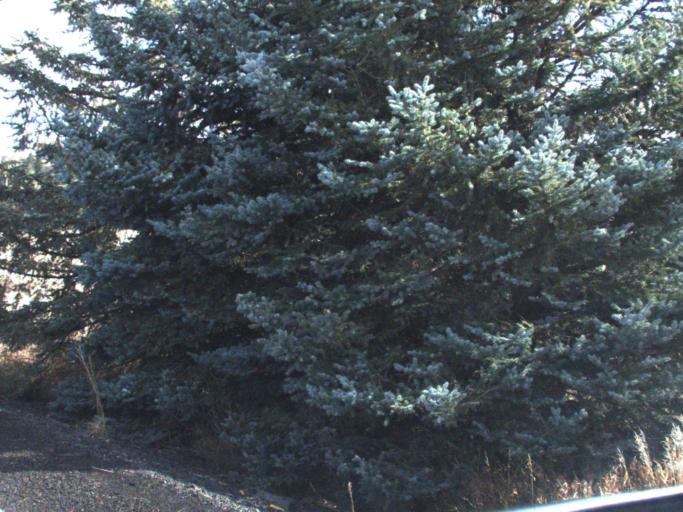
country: US
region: Idaho
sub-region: Latah County
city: Moscow
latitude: 46.9163
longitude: -117.0898
